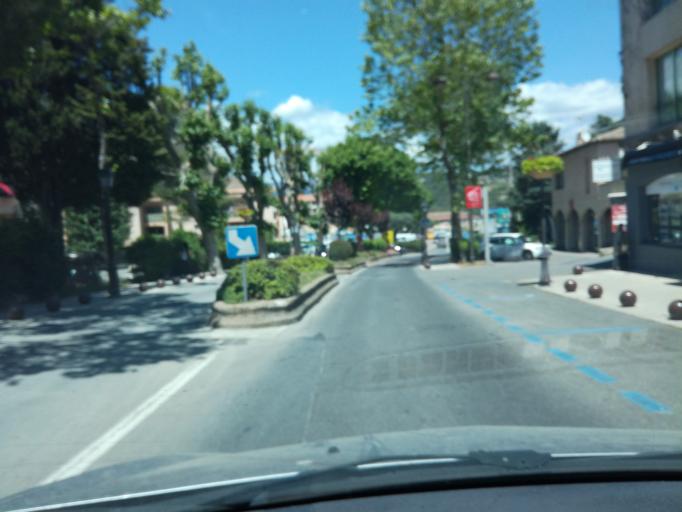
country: FR
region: Provence-Alpes-Cote d'Azur
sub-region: Departement des Alpes-Maritimes
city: Mougins
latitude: 43.5999
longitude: 6.9861
